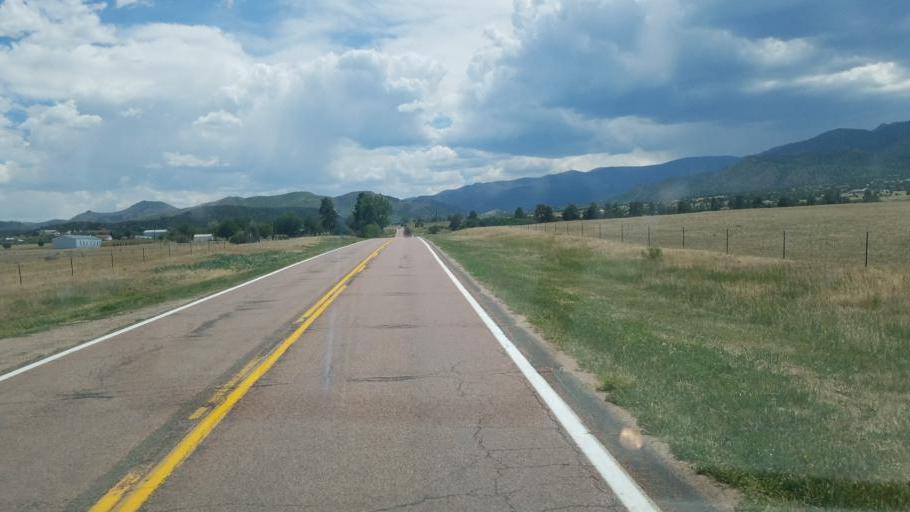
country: US
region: Colorado
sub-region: Fremont County
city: Florence
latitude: 38.2501
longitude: -105.0904
